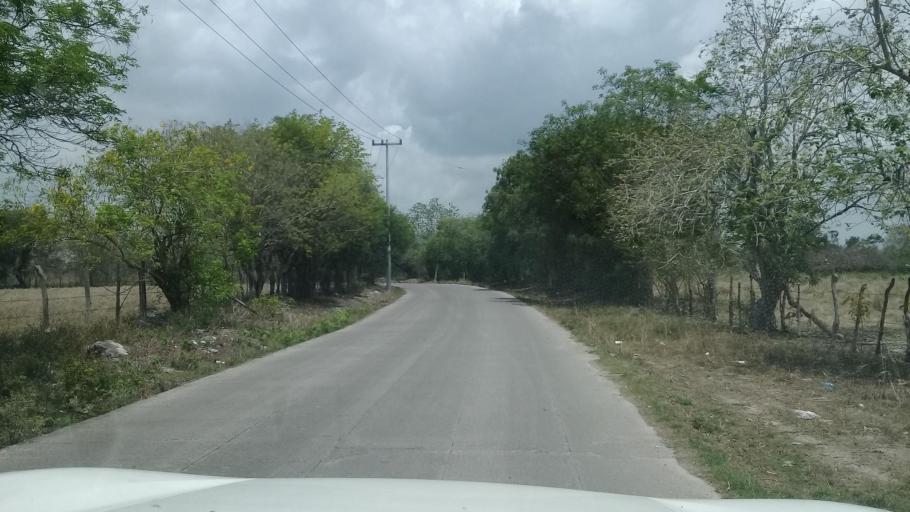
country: MX
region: Veracruz
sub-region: Emiliano Zapata
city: Plan del Rio
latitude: 19.3550
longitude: -96.6493
